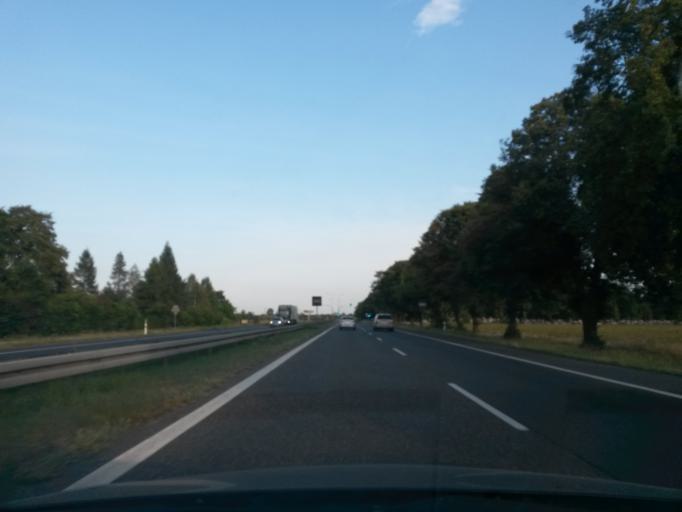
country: PL
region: Masovian Voivodeship
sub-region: Powiat plonski
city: Zaluski
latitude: 52.4826
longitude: 20.5537
